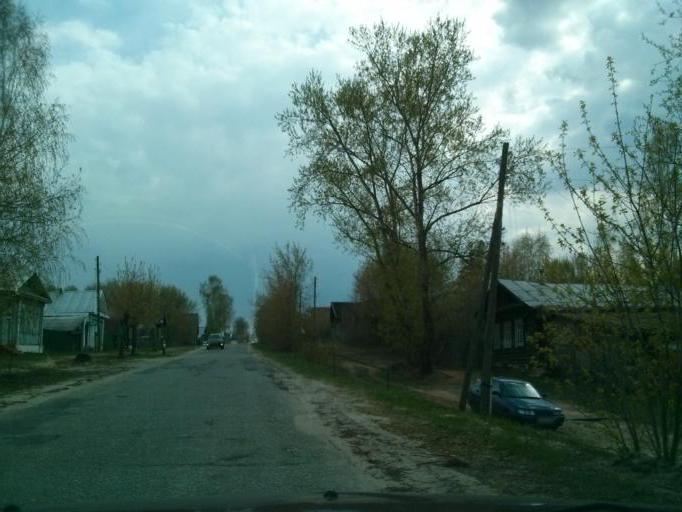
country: RU
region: Nizjnij Novgorod
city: Shimorskoye
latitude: 55.3635
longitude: 41.9332
